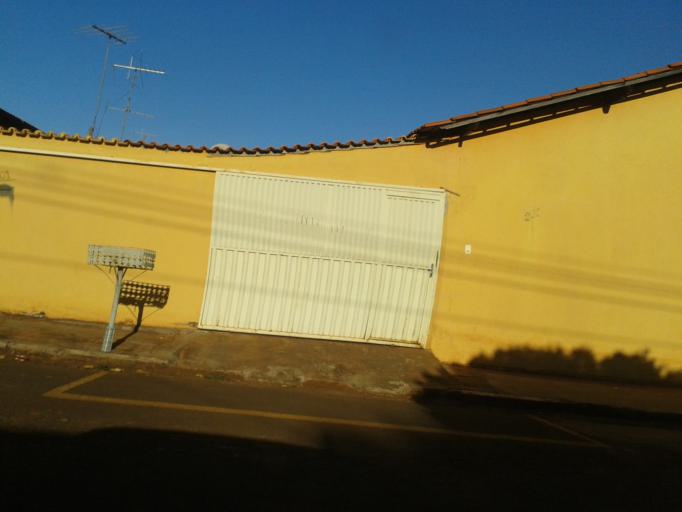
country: BR
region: Minas Gerais
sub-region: Centralina
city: Centralina
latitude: -18.7262
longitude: -49.2066
